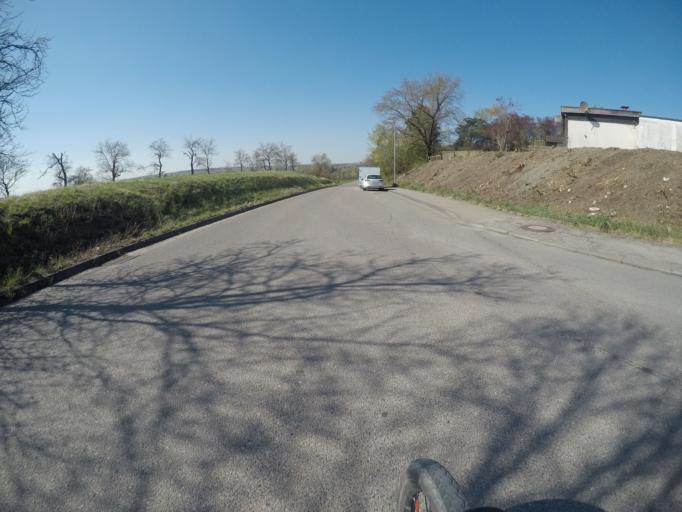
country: DE
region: Baden-Wuerttemberg
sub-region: Regierungsbezirk Stuttgart
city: Herrenberg
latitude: 48.5629
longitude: 8.9176
